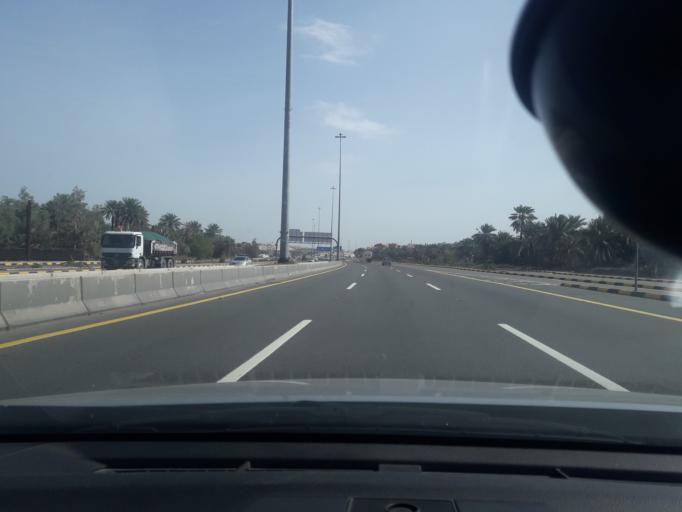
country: SA
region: Al Madinah al Munawwarah
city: Medina
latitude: 24.4414
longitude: 39.6303
